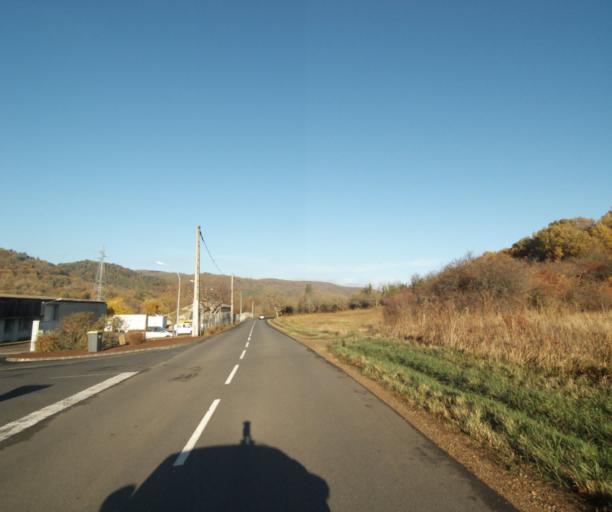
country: FR
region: Auvergne
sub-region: Departement du Puy-de-Dome
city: Durtol
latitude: 45.7983
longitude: 3.0582
